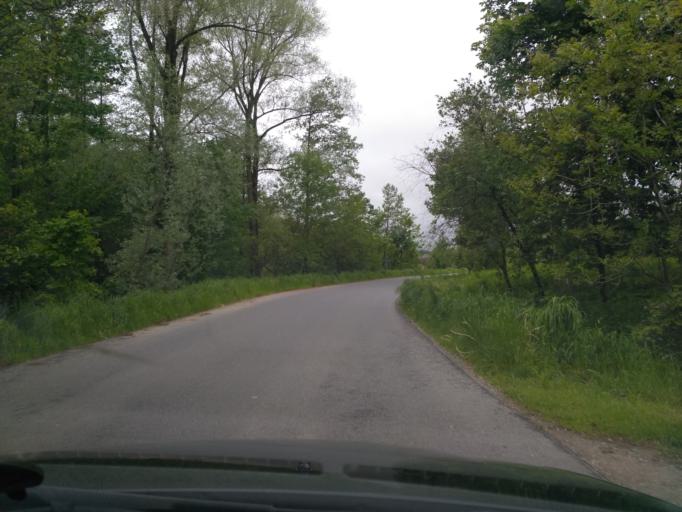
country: PL
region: Subcarpathian Voivodeship
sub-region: Powiat jasielski
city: Brzyska
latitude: 49.8530
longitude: 21.3487
